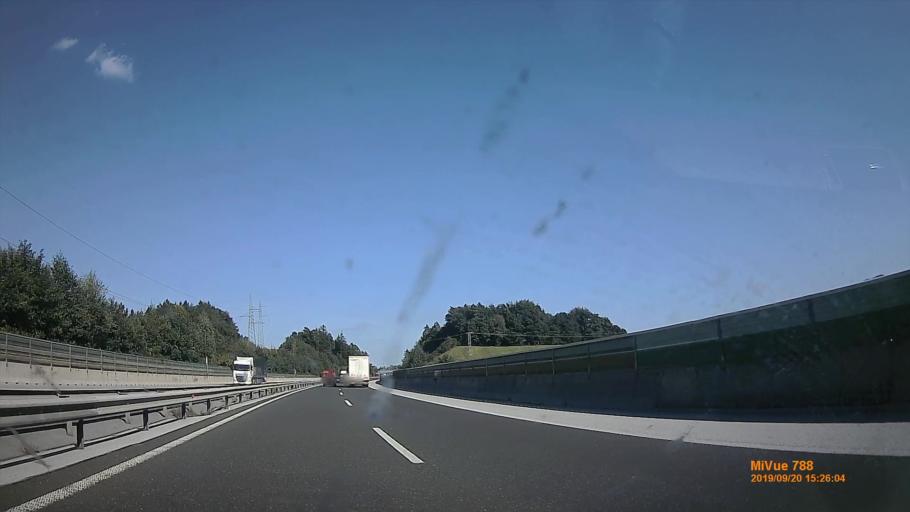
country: SI
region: Vransko
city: Vransko
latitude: 46.2557
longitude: 14.9816
